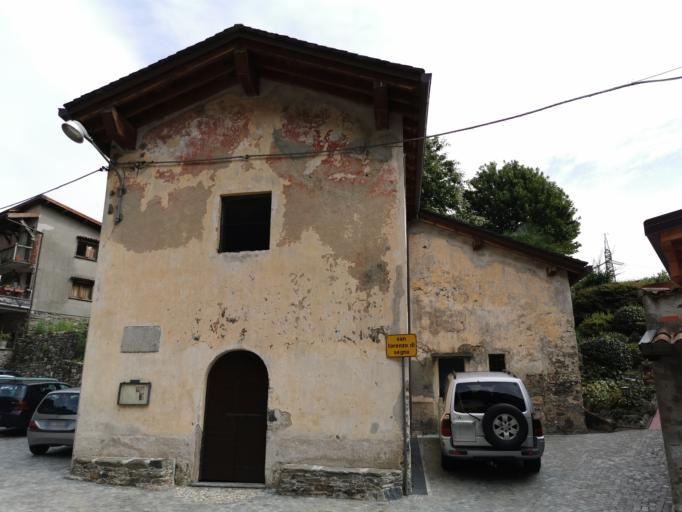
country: IT
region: Lombardy
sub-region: Provincia di Como
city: Gravedona-San Gregorio
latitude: 46.1524
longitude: 9.3152
